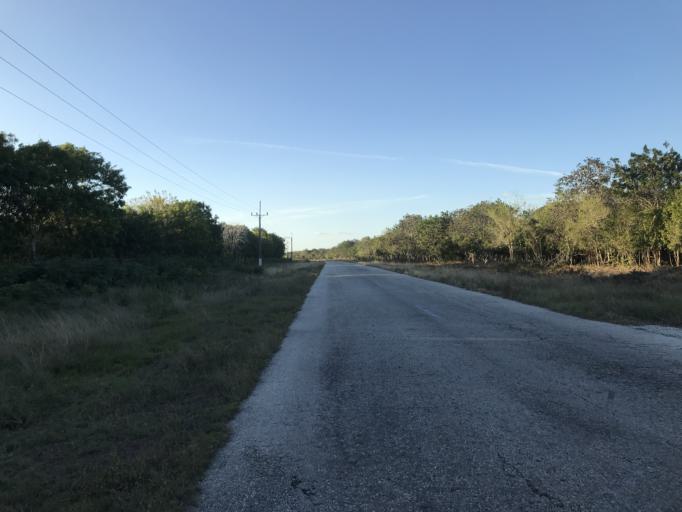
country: CU
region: Cienfuegos
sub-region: Municipio de Aguada de Pasajeros
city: Aguada de Pasajeros
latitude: 22.0715
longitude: -81.0548
